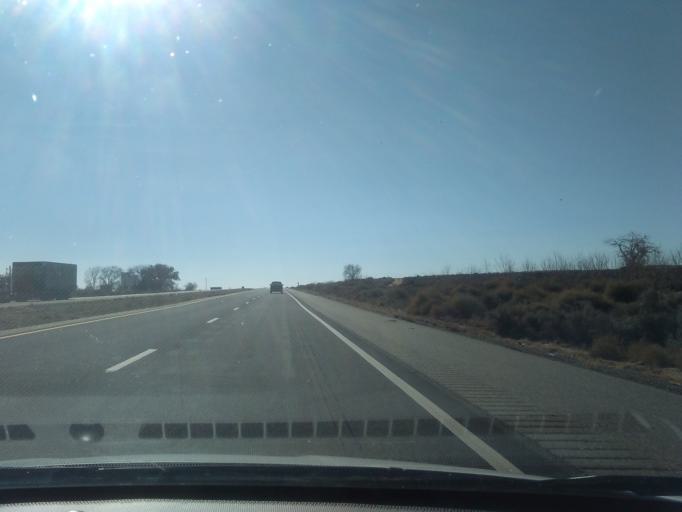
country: US
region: New Mexico
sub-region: Valencia County
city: Jarales
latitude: 34.6160
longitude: -106.7851
